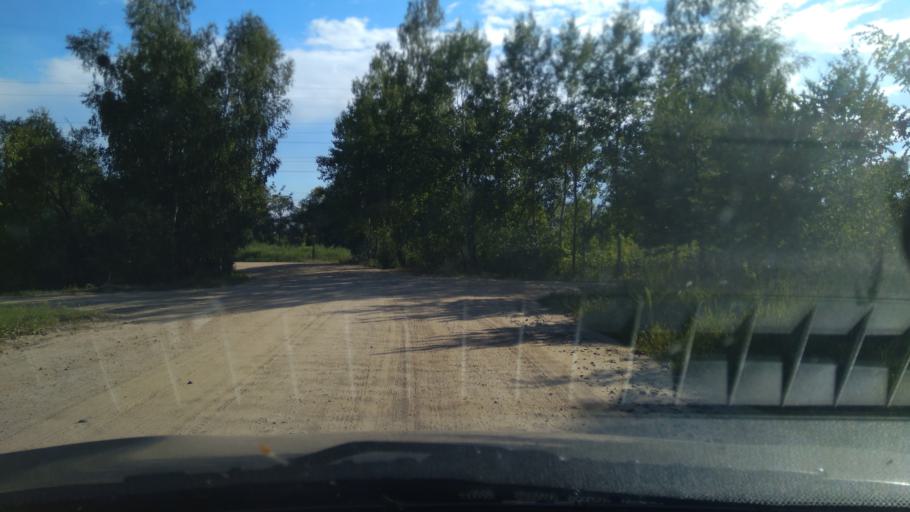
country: BY
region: Brest
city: Byelaazyorsk
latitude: 52.4527
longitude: 25.1838
